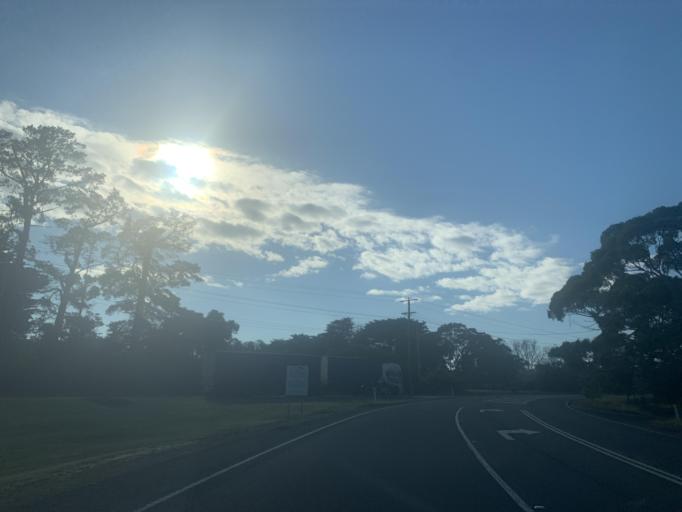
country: AU
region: Victoria
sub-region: Mornington Peninsula
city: Hastings
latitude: -38.2879
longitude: 145.1965
